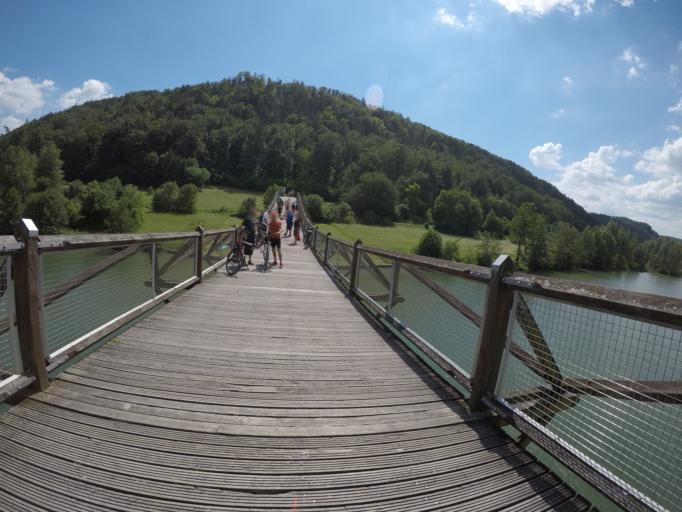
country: DE
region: Bavaria
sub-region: Lower Bavaria
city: Essing
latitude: 48.9384
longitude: 11.7808
